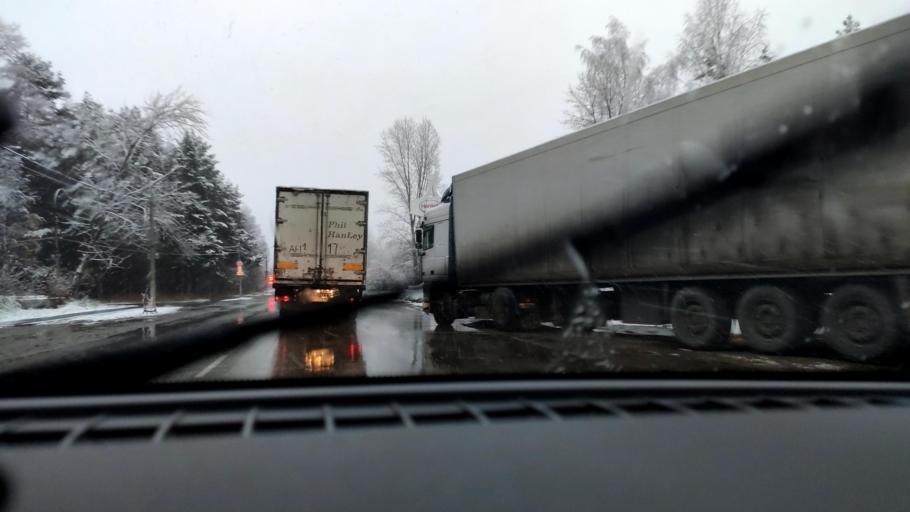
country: RU
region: Perm
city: Overyata
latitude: 58.0132
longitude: 55.9183
